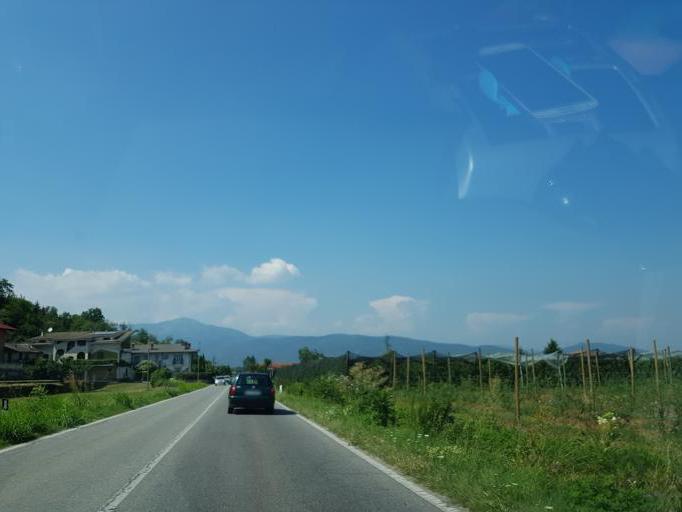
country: IT
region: Piedmont
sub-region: Provincia di Cuneo
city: Caraglio
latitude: 44.4272
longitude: 7.4264
